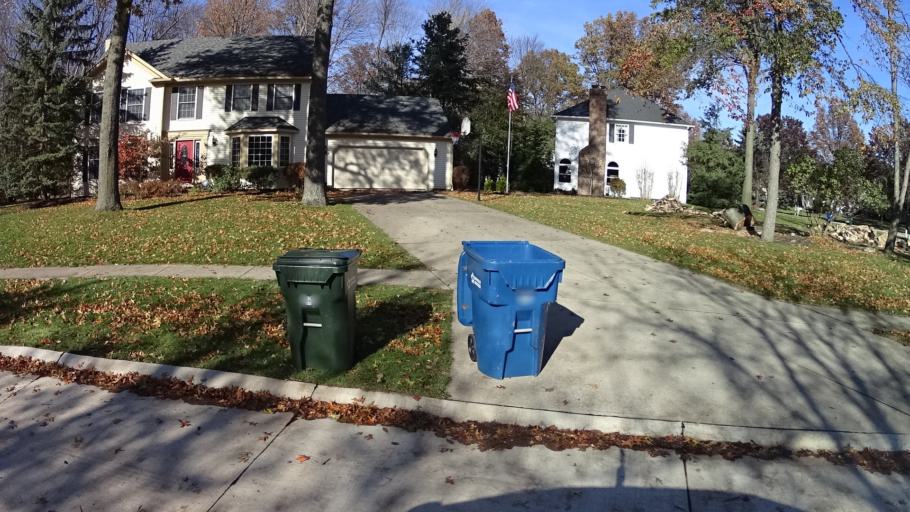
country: US
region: Ohio
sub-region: Lorain County
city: Avon Lake
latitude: 41.4951
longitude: -81.9962
